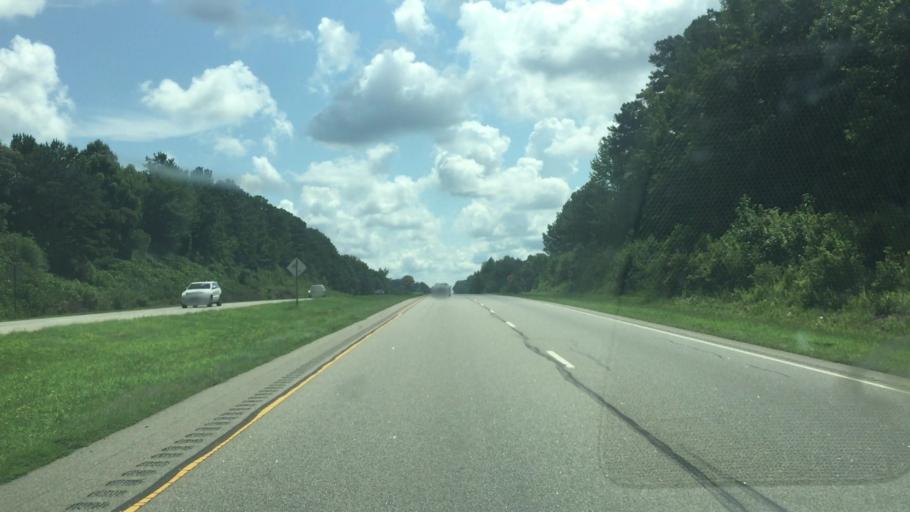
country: US
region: North Carolina
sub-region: Anson County
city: Wadesboro
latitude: 34.9633
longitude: -80.0136
